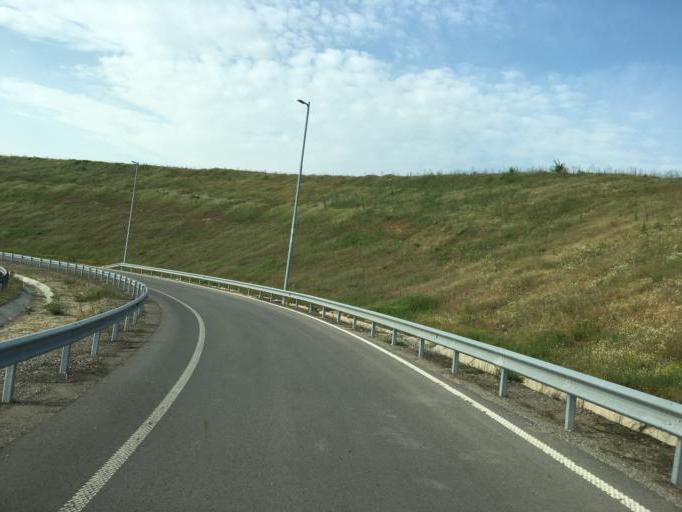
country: BG
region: Kyustendil
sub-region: Obshtina Kocherinovo
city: Kocherinovo
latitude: 42.0549
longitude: 23.0467
